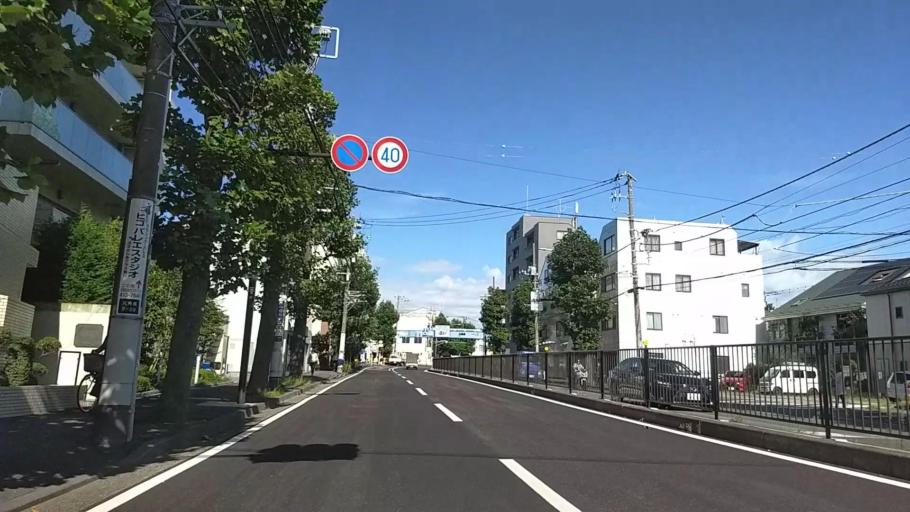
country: JP
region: Kanagawa
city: Yokohama
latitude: 35.4898
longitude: 139.6225
